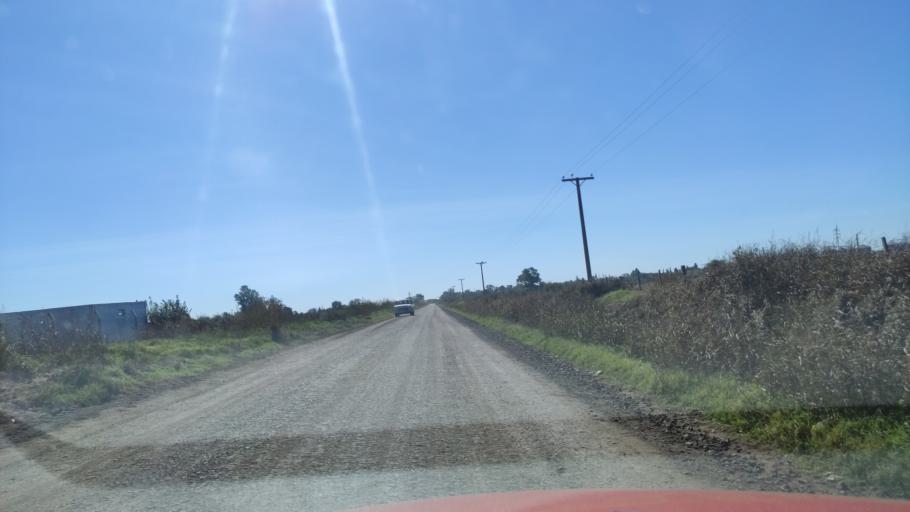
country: AR
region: Cordoba
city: Leones
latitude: -32.6710
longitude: -62.3127
